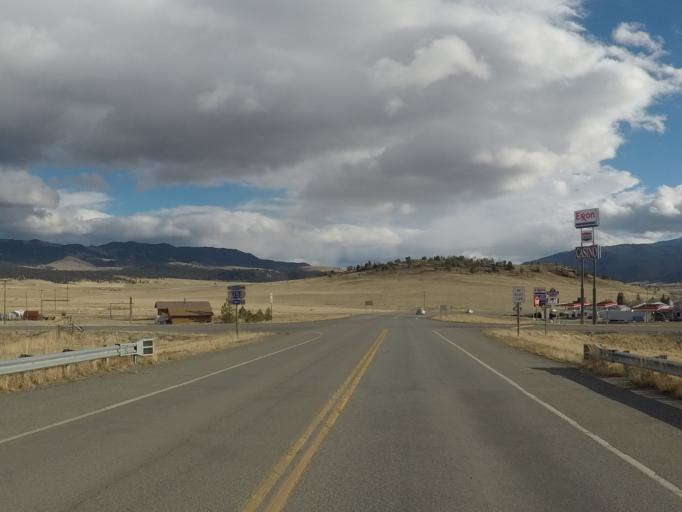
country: US
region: Montana
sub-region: Jefferson County
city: Boulder
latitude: 46.2462
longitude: -112.1184
